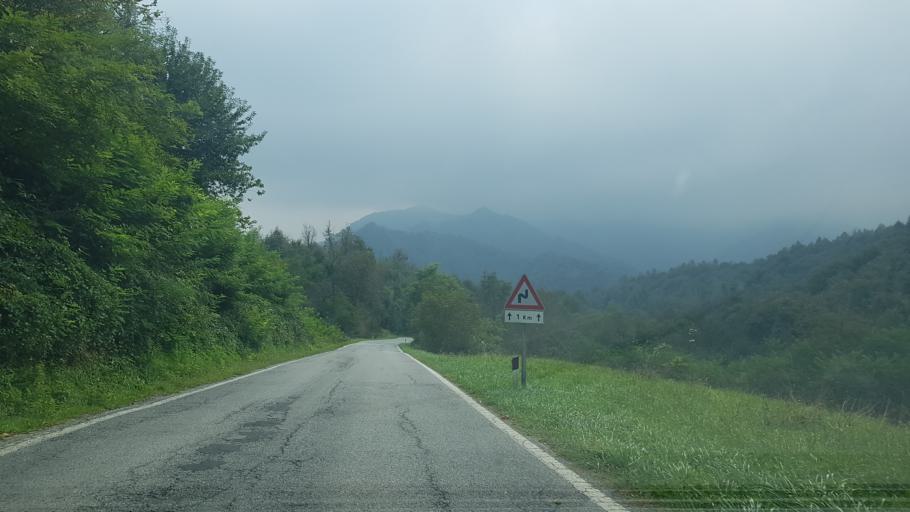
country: IT
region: Piedmont
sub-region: Provincia di Cuneo
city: Chiusa di Pesio
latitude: 44.3131
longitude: 7.7073
